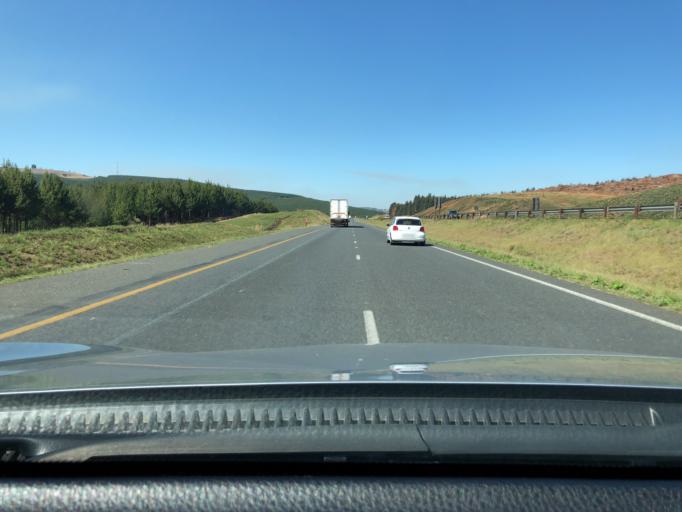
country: ZA
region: KwaZulu-Natal
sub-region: uMgungundlovu District Municipality
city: Howick
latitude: -29.3801
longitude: 30.1272
